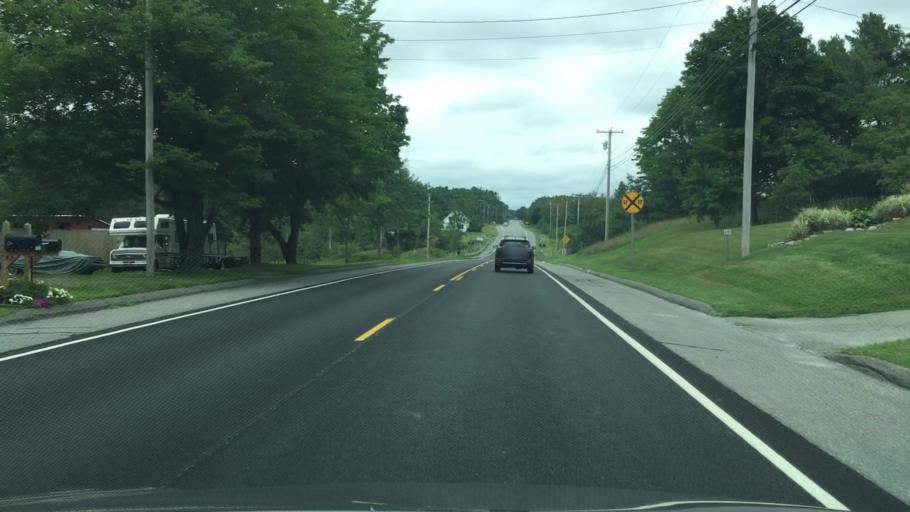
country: US
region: Maine
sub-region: Penobscot County
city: Orrington
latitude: 44.7009
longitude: -68.8211
